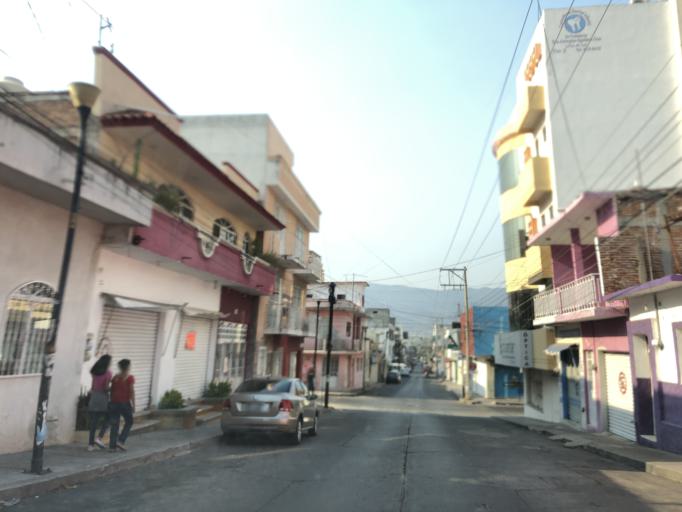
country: MX
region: Chiapas
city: Tuxtla Gutierrez
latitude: 16.7522
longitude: -93.1217
